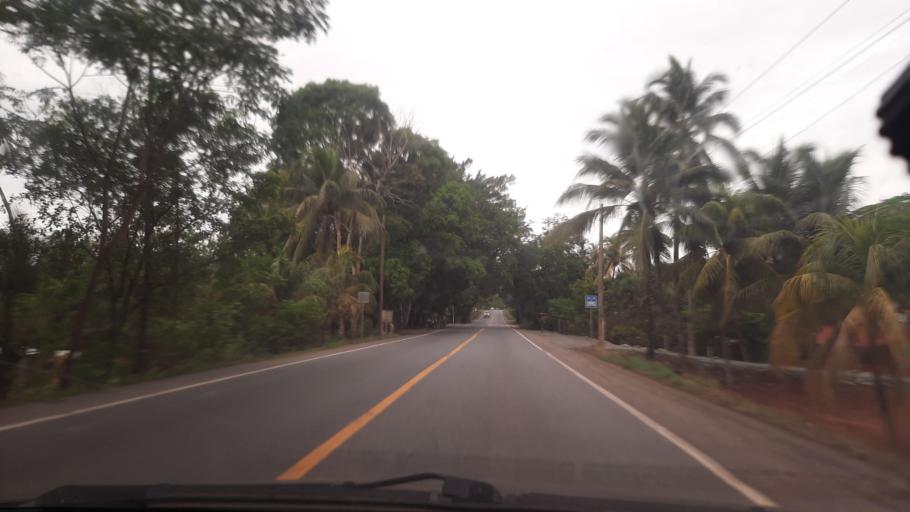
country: GT
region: Izabal
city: Morales
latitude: 15.4276
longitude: -88.9777
